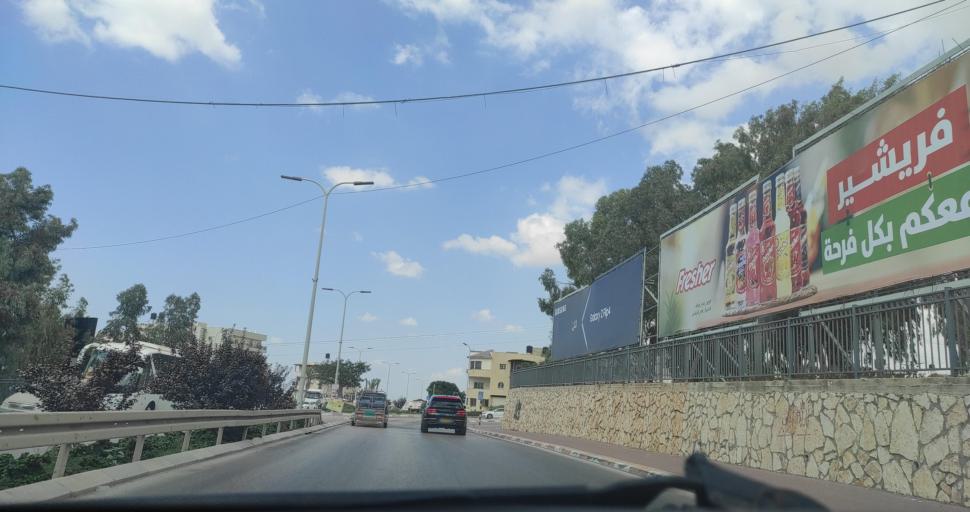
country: IL
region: Central District
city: Kafr Qasim
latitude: 32.1168
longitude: 34.9638
